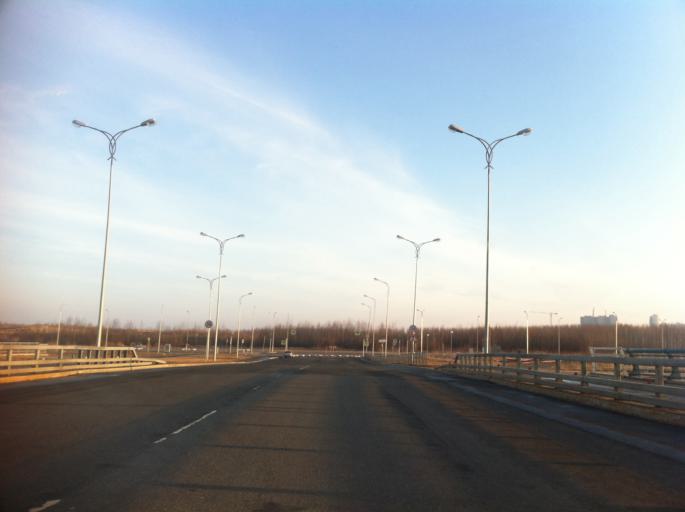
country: RU
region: St.-Petersburg
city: Sosnovaya Polyana
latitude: 59.8559
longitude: 30.1472
